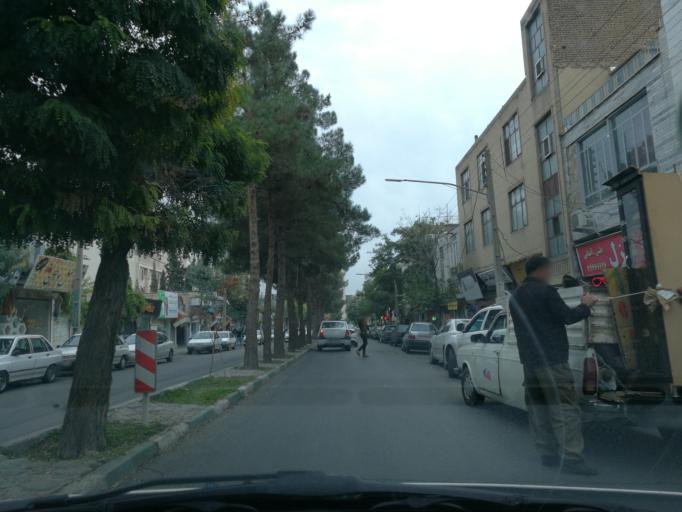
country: IR
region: Alborz
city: Karaj
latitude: 35.8469
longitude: 50.9695
